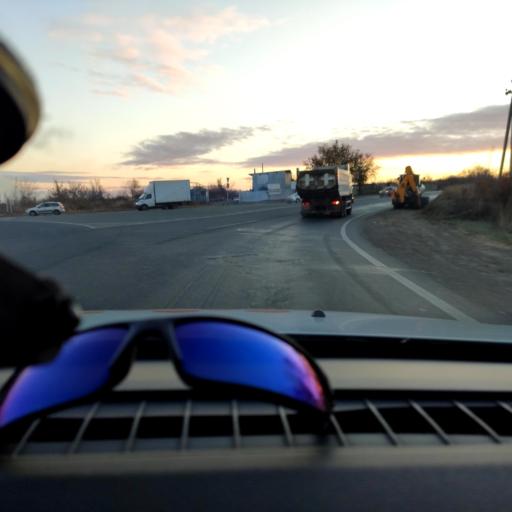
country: RU
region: Samara
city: Novokuybyshevsk
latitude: 53.0855
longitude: 50.0619
